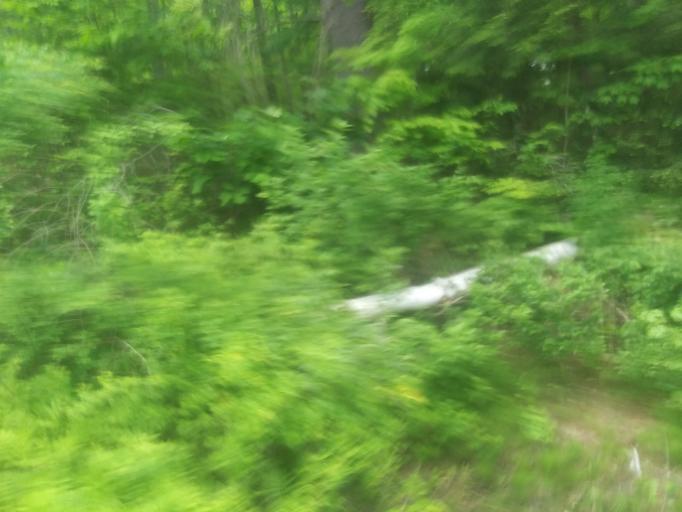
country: US
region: Massachusetts
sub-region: Franklin County
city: Shelburne Falls
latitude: 42.5979
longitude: -72.7443
